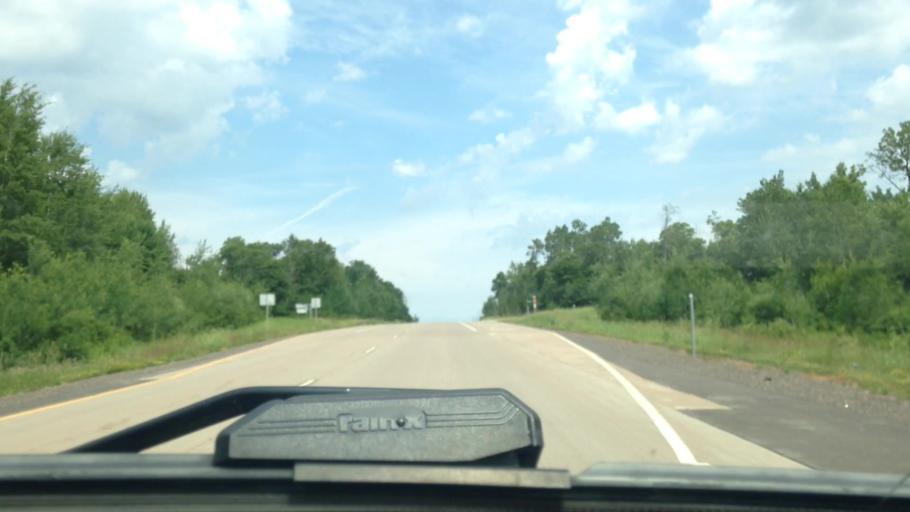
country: US
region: Wisconsin
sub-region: Douglas County
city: Lake Nebagamon
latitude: 46.2725
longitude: -91.8048
